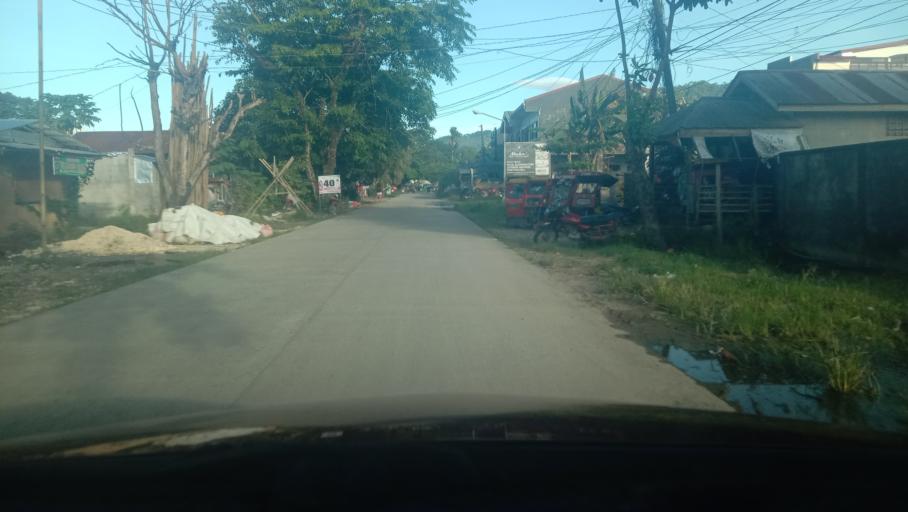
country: PH
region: Caraga
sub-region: Province of Agusan del Sur
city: San Francisco
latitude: 8.5109
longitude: 125.9738
